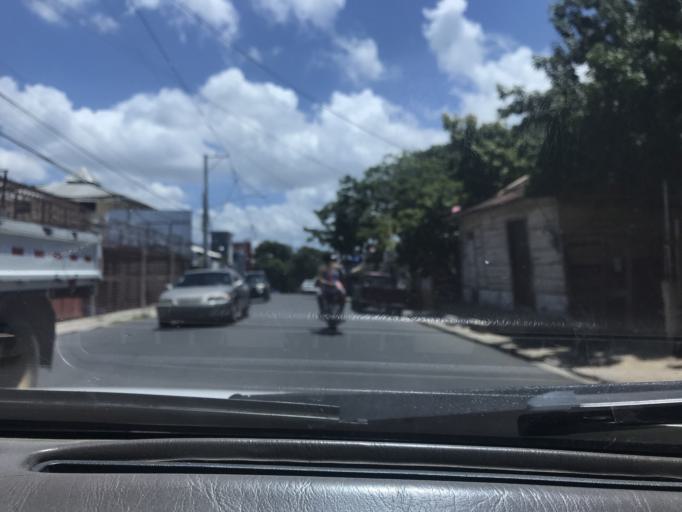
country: DO
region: Santiago
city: Santiago de los Caballeros
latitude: 19.4309
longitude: -70.6959
